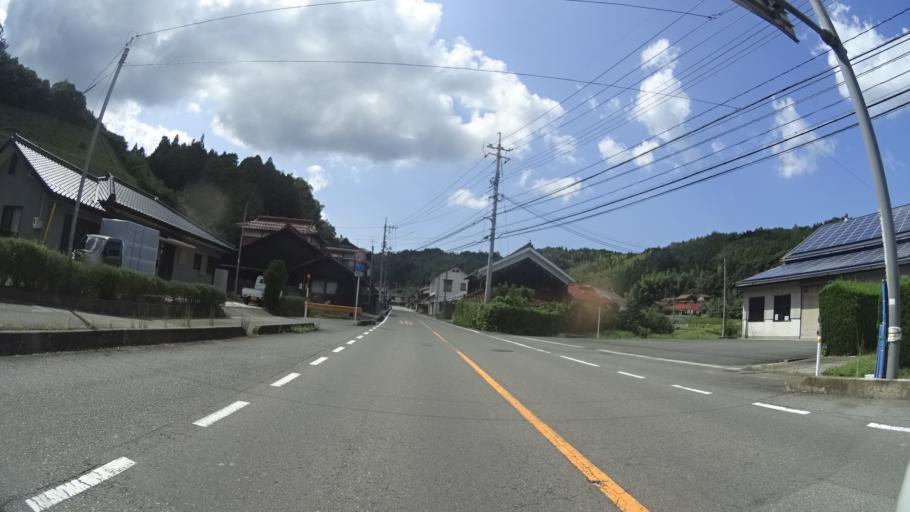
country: JP
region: Yamaguchi
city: Hagi
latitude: 34.4351
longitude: 131.4813
